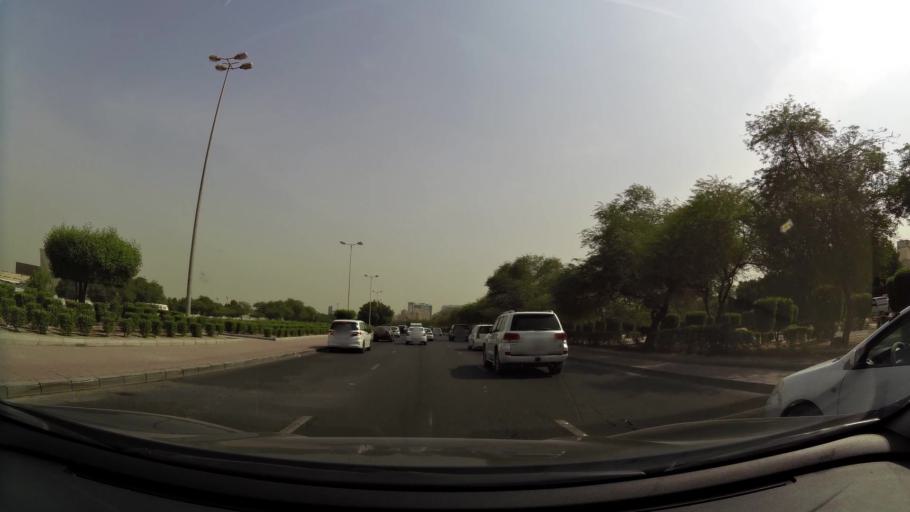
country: KW
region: Al Asimah
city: Ar Rabiyah
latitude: 29.3066
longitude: 47.8969
